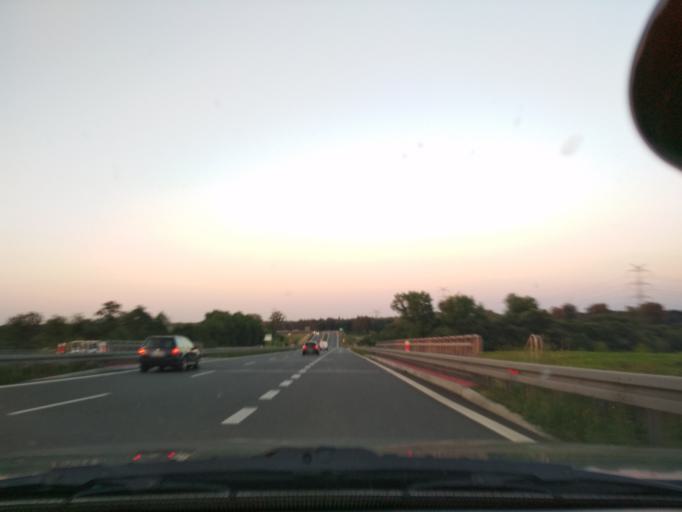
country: PL
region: Silesian Voivodeship
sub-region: Powiat bedzinski
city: Siewierz
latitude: 50.4606
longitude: 19.2367
